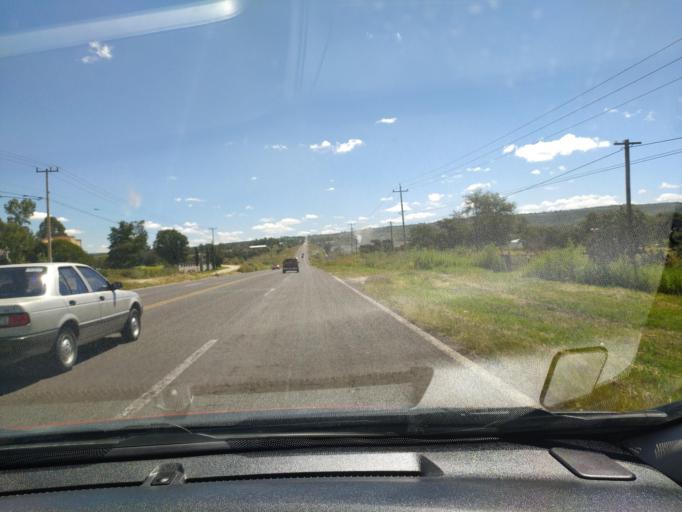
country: MX
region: Jalisco
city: San Miguel el Alto
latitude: 21.0240
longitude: -102.3653
